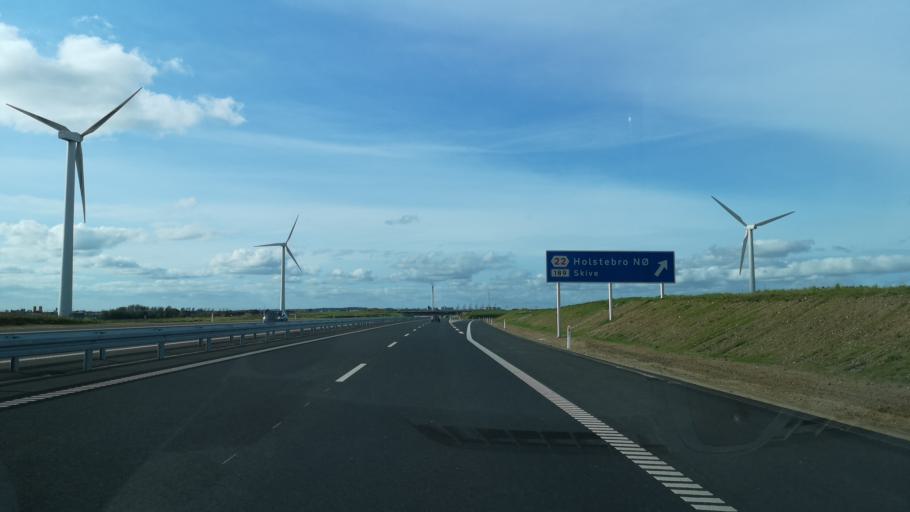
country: DK
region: Central Jutland
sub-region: Holstebro Kommune
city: Holstebro
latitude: 56.3835
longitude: 8.6635
